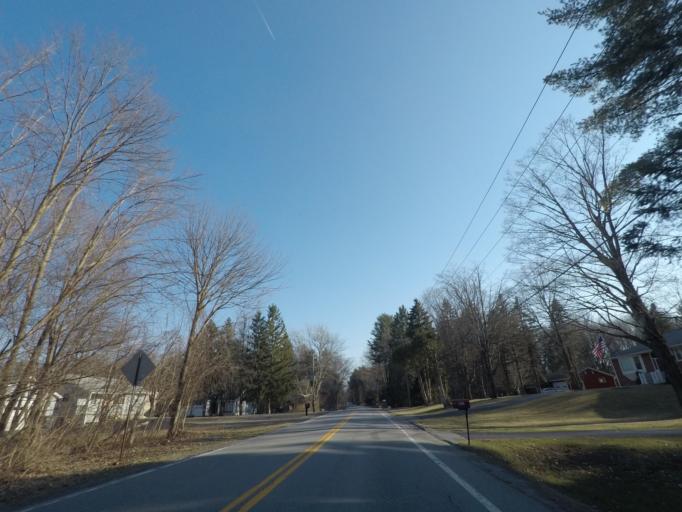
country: US
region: New York
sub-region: Saratoga County
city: Country Knolls
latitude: 42.8384
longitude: -73.7765
